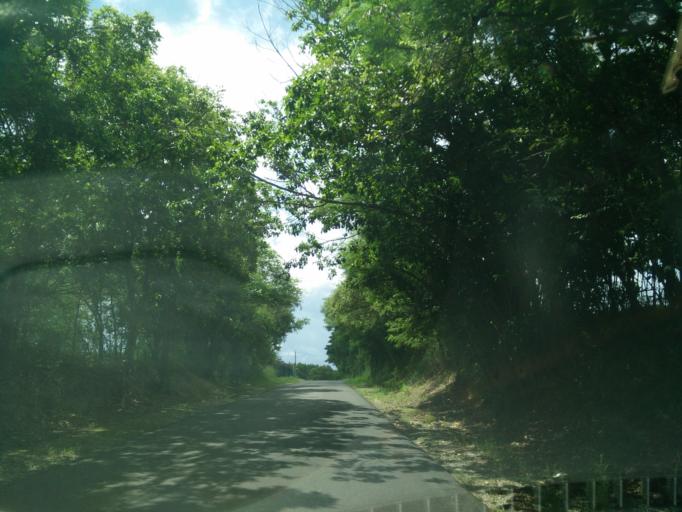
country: GP
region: Guadeloupe
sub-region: Guadeloupe
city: Le Moule
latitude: 16.3080
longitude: -61.3222
